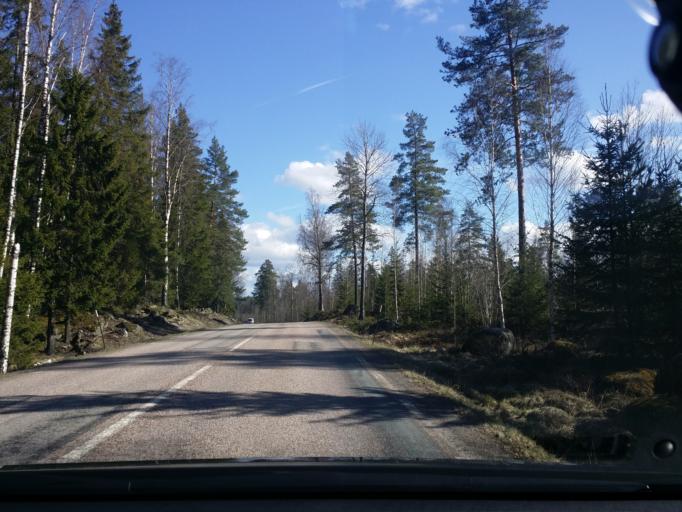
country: SE
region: Vaestmanland
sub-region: Sala Kommun
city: Sala
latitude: 59.9740
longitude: 16.4984
